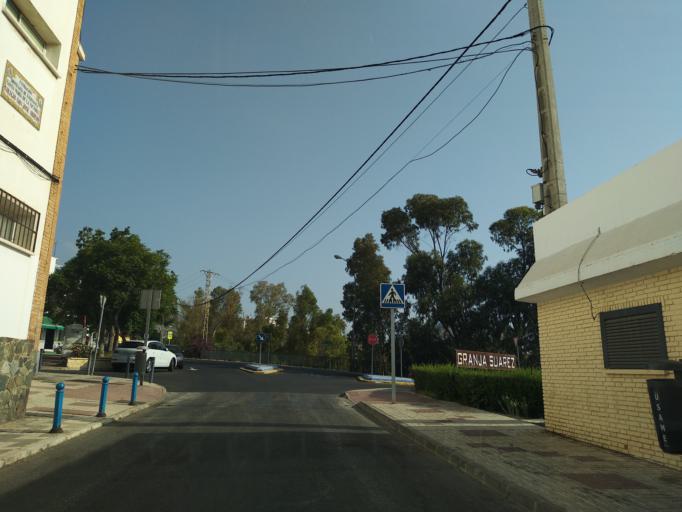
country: ES
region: Andalusia
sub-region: Provincia de Malaga
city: Malaga
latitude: 36.7277
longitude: -4.4499
